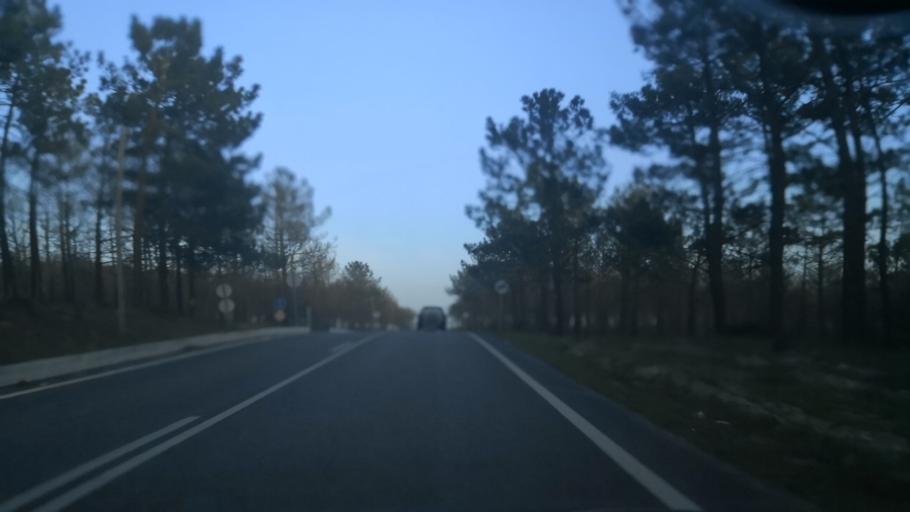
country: PT
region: Leiria
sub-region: Marinha Grande
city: Marinha Grande
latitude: 39.7511
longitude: -9.0158
